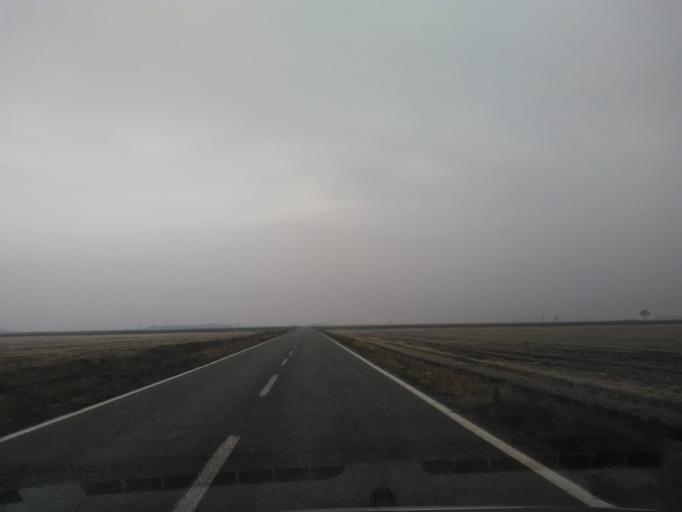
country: IT
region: Piedmont
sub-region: Provincia di Vercelli
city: Salasco
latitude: 45.2968
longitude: 8.2795
